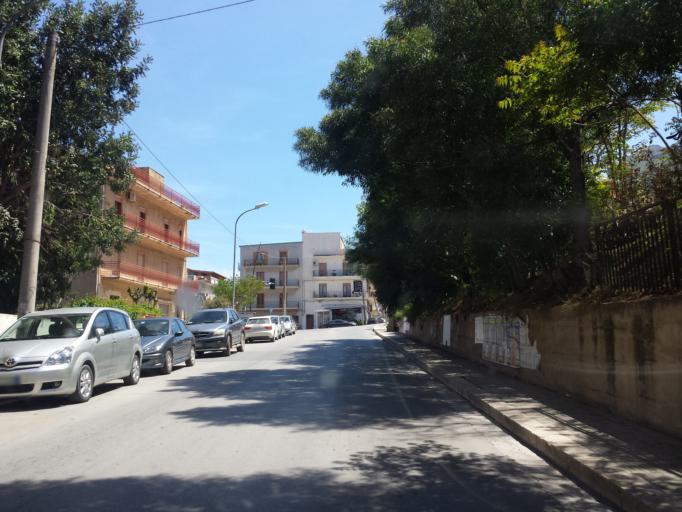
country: IT
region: Sicily
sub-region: Trapani
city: Castellammare del Golfo
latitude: 38.0183
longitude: 12.8844
